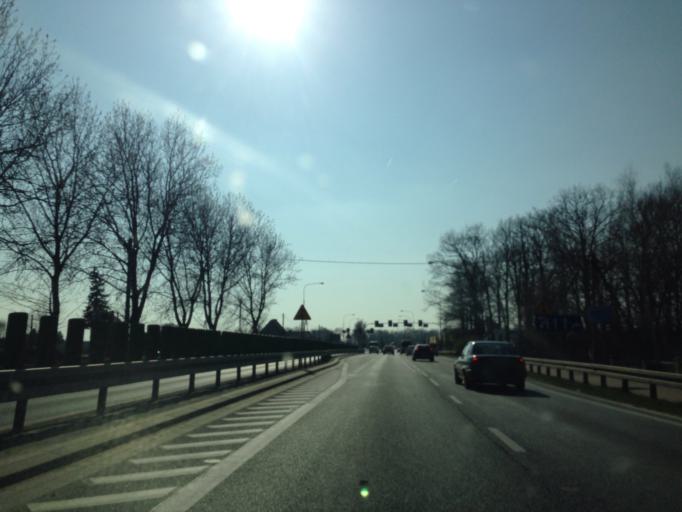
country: PL
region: Lower Silesian Voivodeship
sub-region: Powiat wroclawski
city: Dlugoleka
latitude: 51.1814
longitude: 17.2023
